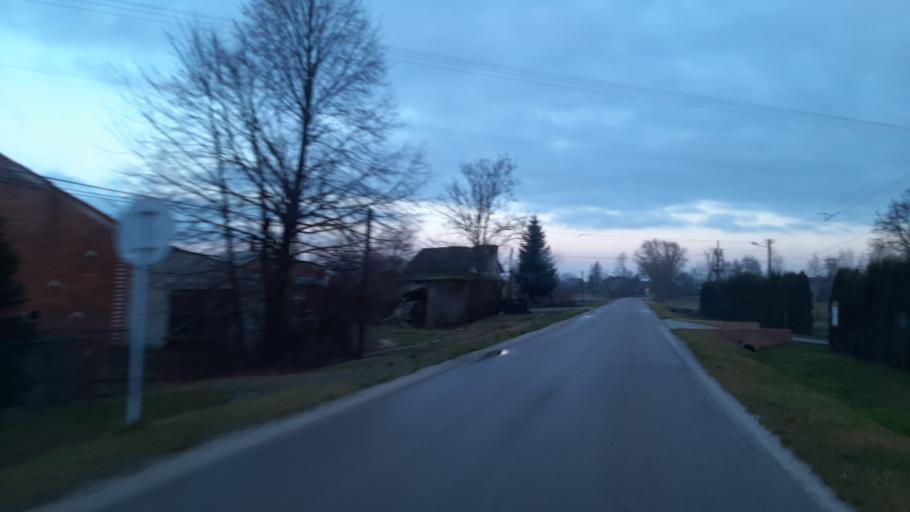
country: PL
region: Lublin Voivodeship
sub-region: Powiat lubartowski
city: Firlej
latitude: 51.5706
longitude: 22.5349
